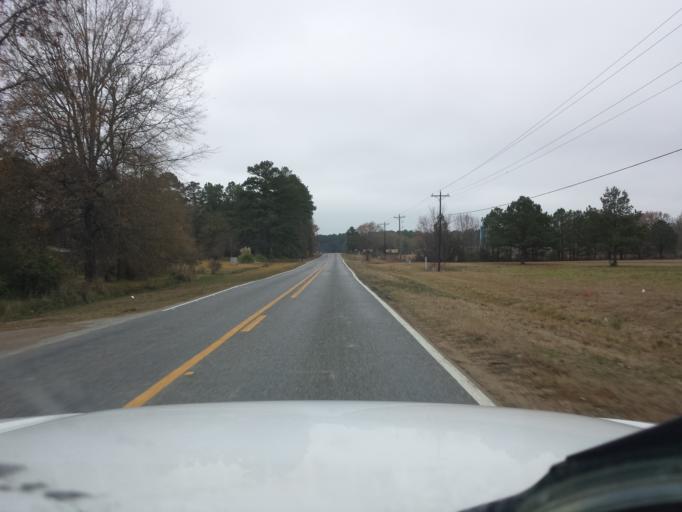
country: US
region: Mississippi
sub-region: Madison County
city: Canton
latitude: 32.4912
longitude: -89.9224
